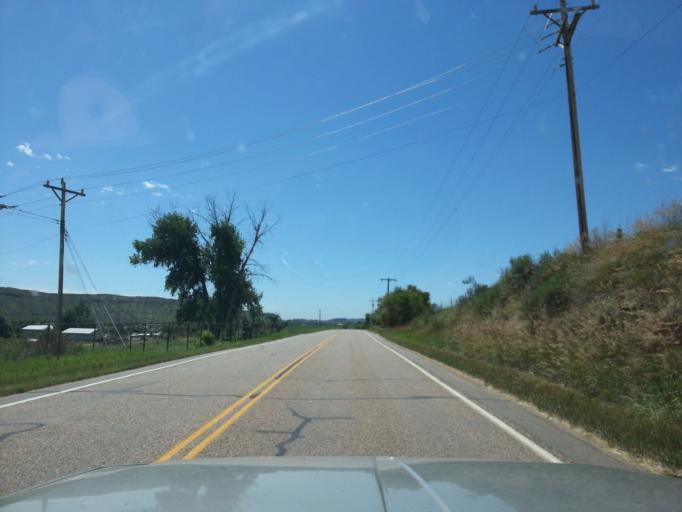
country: US
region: Colorado
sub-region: Larimer County
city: Loveland
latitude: 40.4733
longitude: -105.2128
